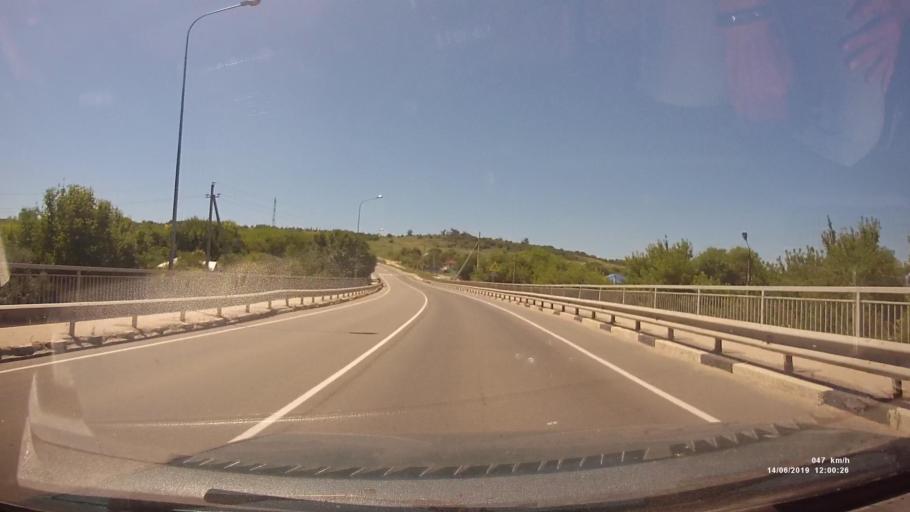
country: RU
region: Rostov
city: Kazanskaya
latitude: 49.7888
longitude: 41.1271
